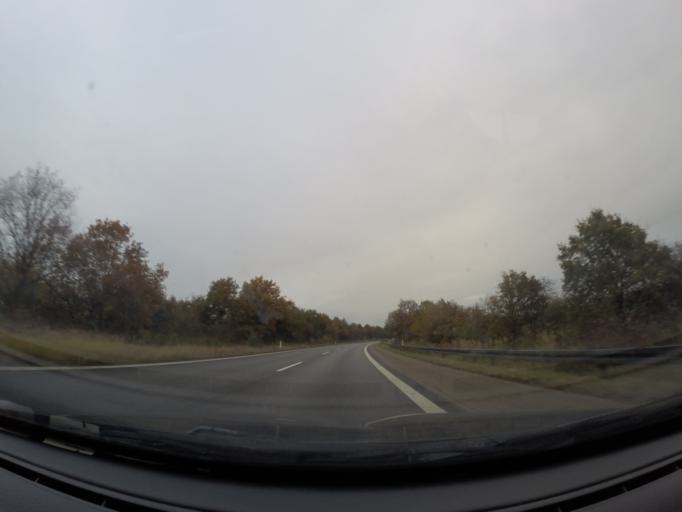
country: DK
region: Capital Region
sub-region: Hoje-Taastrup Kommune
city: Taastrup
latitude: 55.6643
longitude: 12.3139
